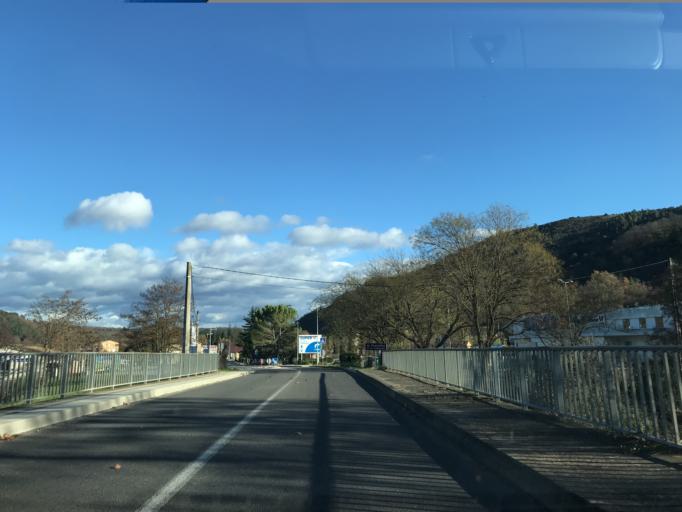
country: FR
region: Rhone-Alpes
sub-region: Departement de l'Ardeche
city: Les Vans
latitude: 44.4137
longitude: 4.1451
